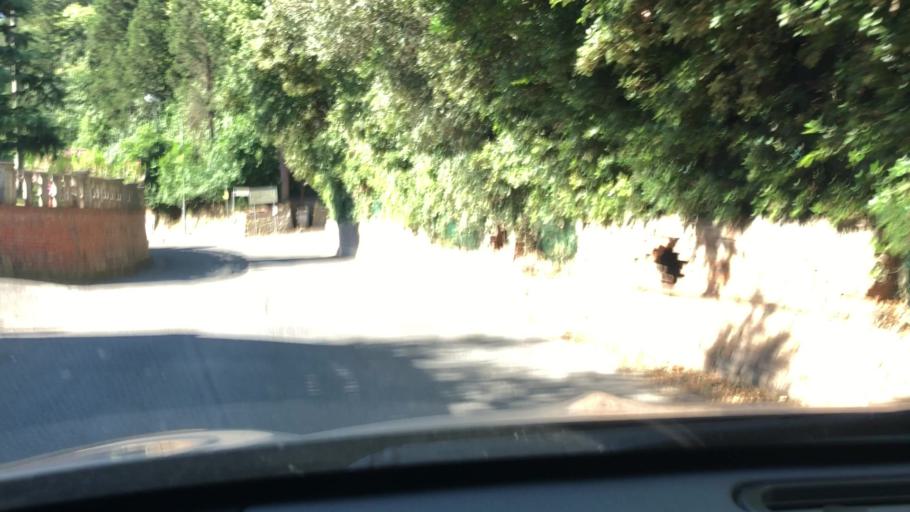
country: IT
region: Tuscany
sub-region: Province of Pisa
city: Forcoli
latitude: 43.6073
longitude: 10.7042
